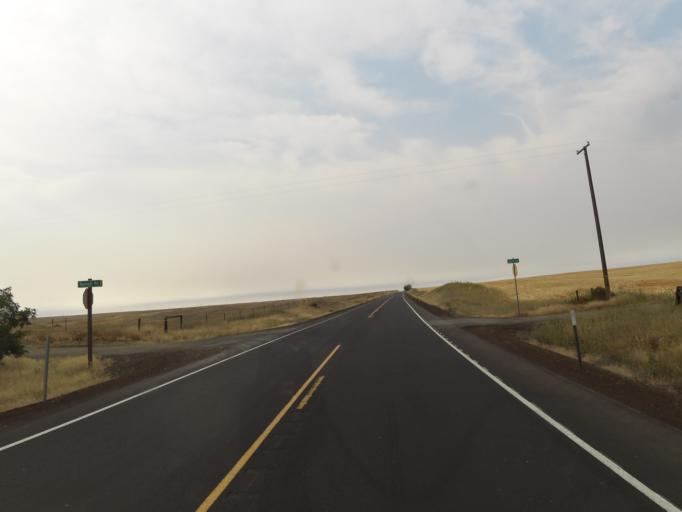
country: US
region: Oregon
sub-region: Sherman County
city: Moro
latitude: 45.3309
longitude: -120.7688
